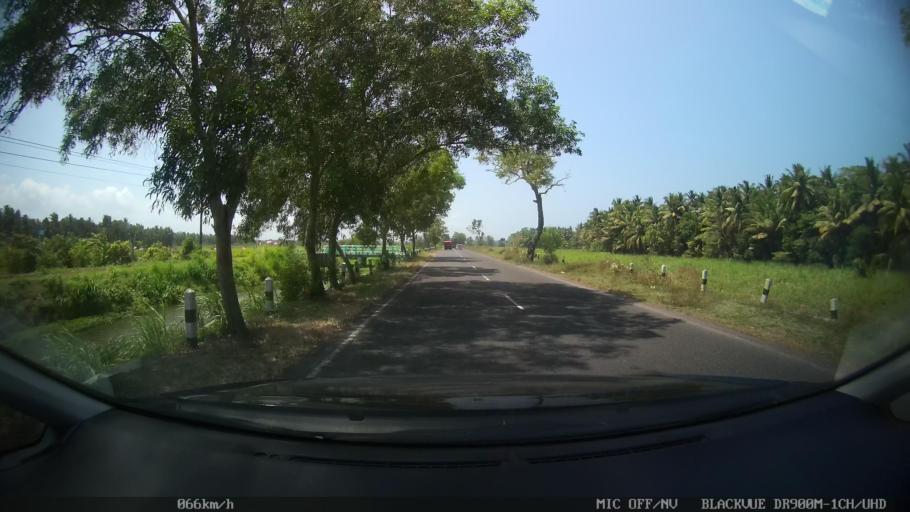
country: ID
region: Daerah Istimewa Yogyakarta
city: Srandakan
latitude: -7.9431
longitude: 110.1664
